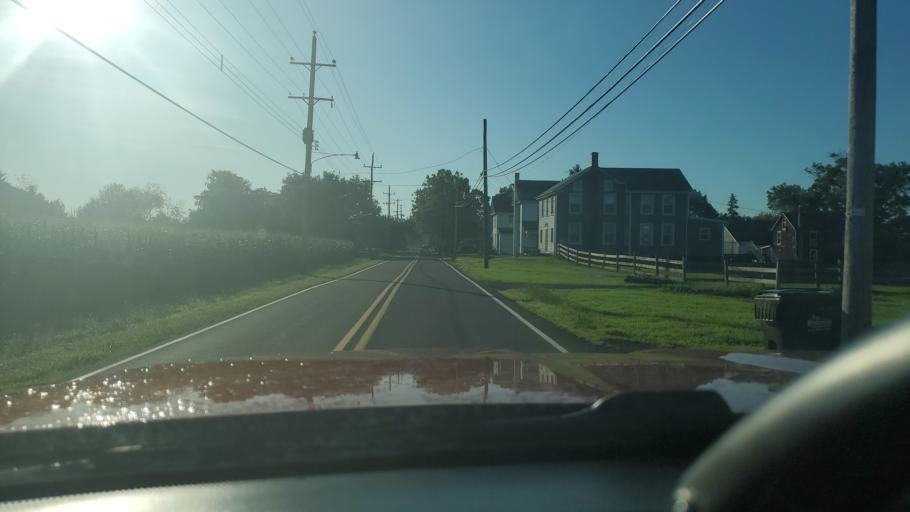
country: US
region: Pennsylvania
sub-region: Montgomery County
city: Woxall
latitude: 40.2950
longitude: -75.4352
